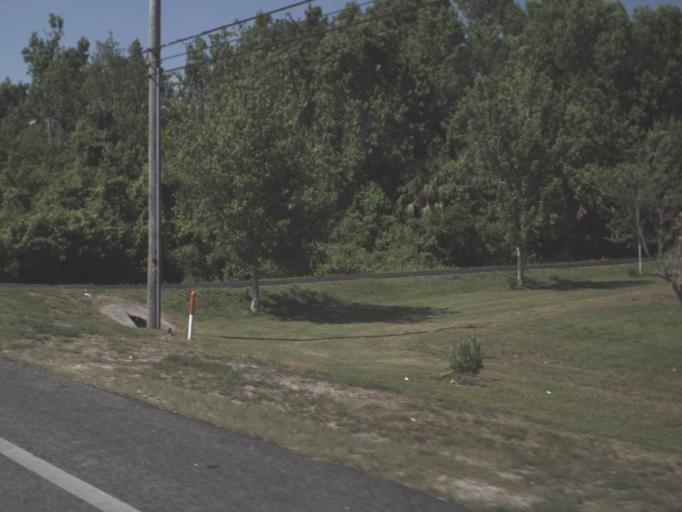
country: US
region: Florida
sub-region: Brevard County
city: Rockledge
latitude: 28.2835
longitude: -80.6958
